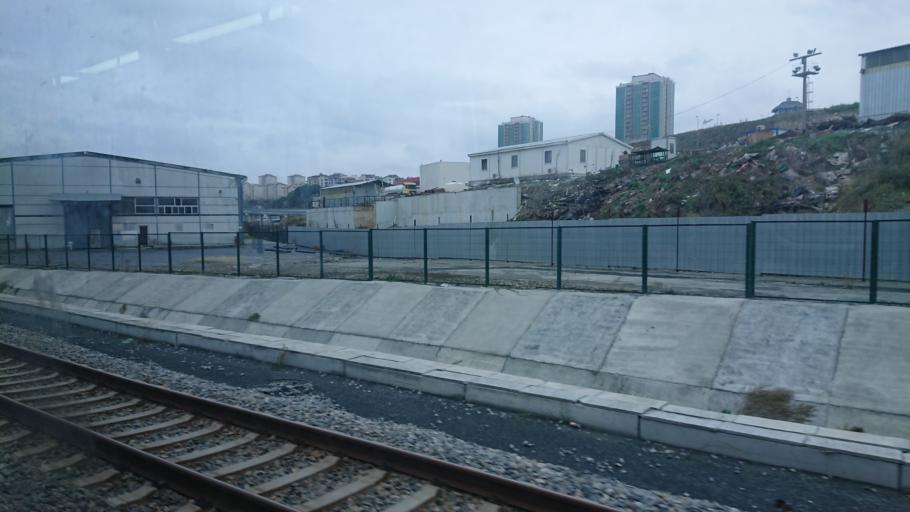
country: TR
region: Istanbul
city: Mahmutbey
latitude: 41.0132
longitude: 28.7673
